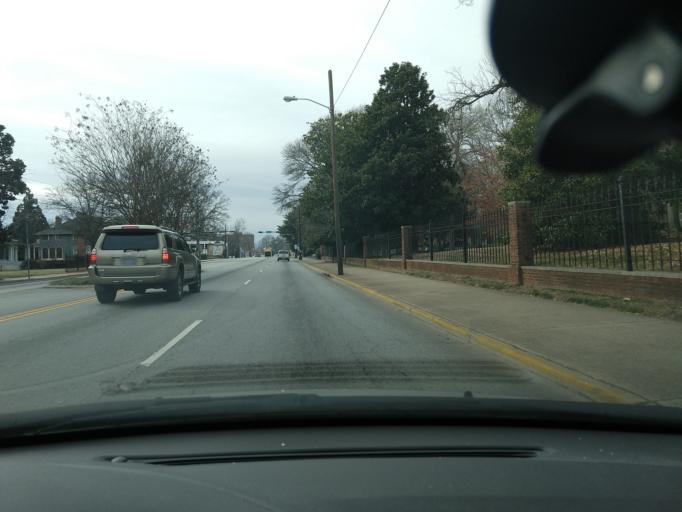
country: US
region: South Carolina
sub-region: Spartanburg County
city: Spartanburg
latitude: 34.9548
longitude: -81.9159
